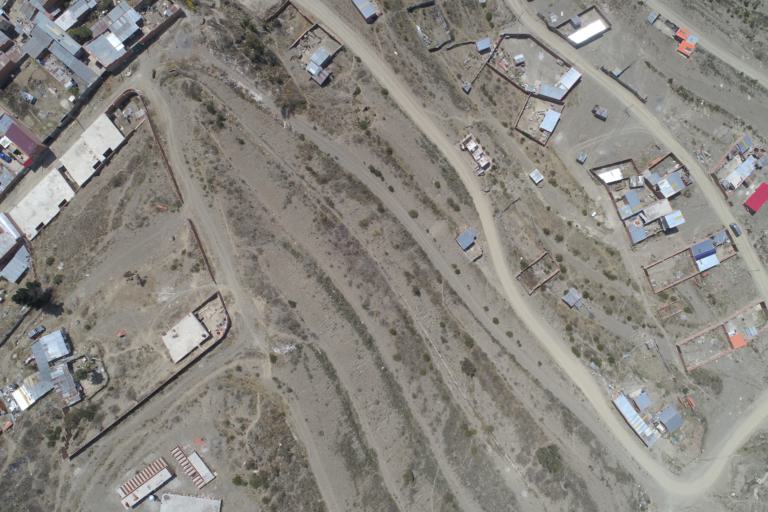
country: BO
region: La Paz
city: La Paz
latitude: -16.5004
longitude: -68.0975
